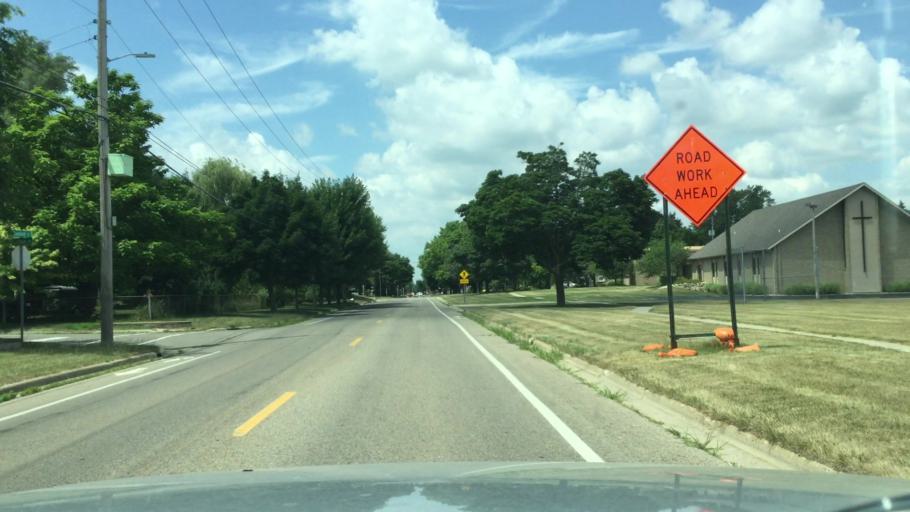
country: US
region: Michigan
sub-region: Genesee County
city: Flushing
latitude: 43.0674
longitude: -83.8264
